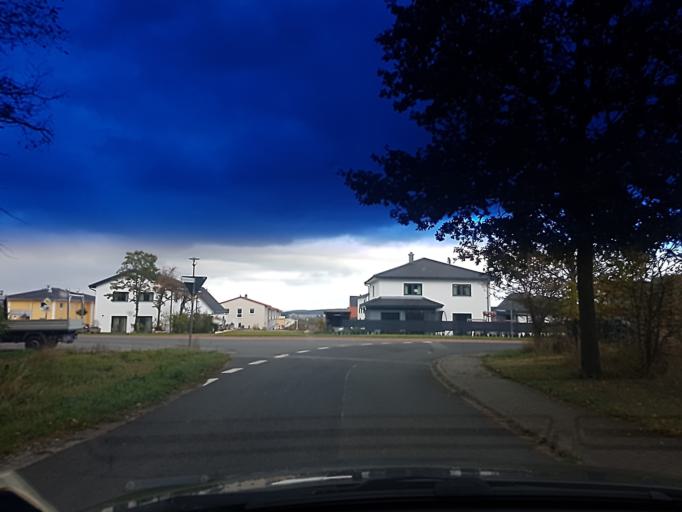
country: DE
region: Bavaria
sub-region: Regierungsbezirk Mittelfranken
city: Burghaslach
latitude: 49.7384
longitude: 10.6049
